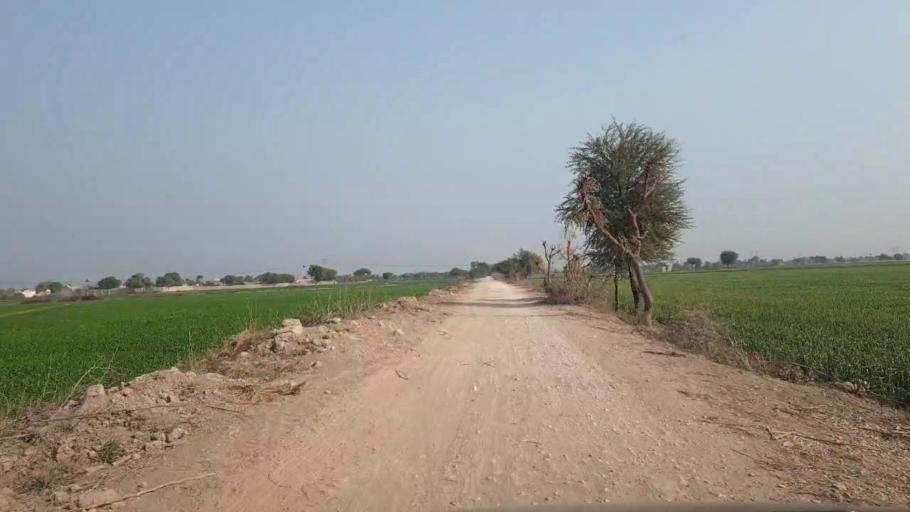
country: PK
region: Sindh
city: Hala
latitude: 25.8830
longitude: 68.4549
